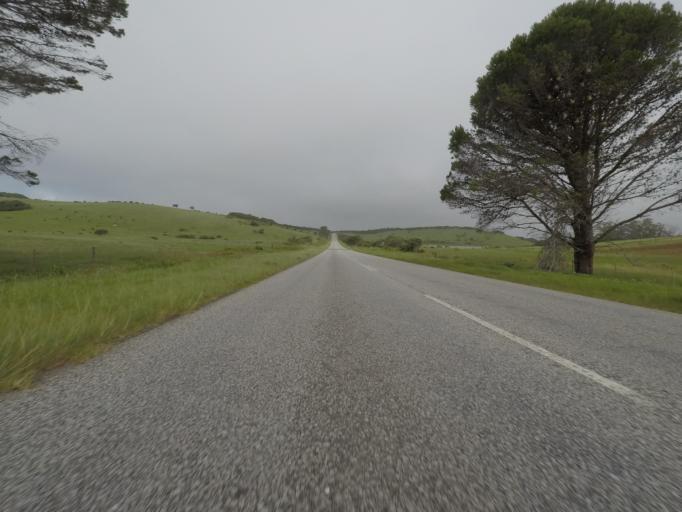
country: ZA
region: Eastern Cape
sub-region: Cacadu District Municipality
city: Port Alfred
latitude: -33.6059
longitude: 26.8326
